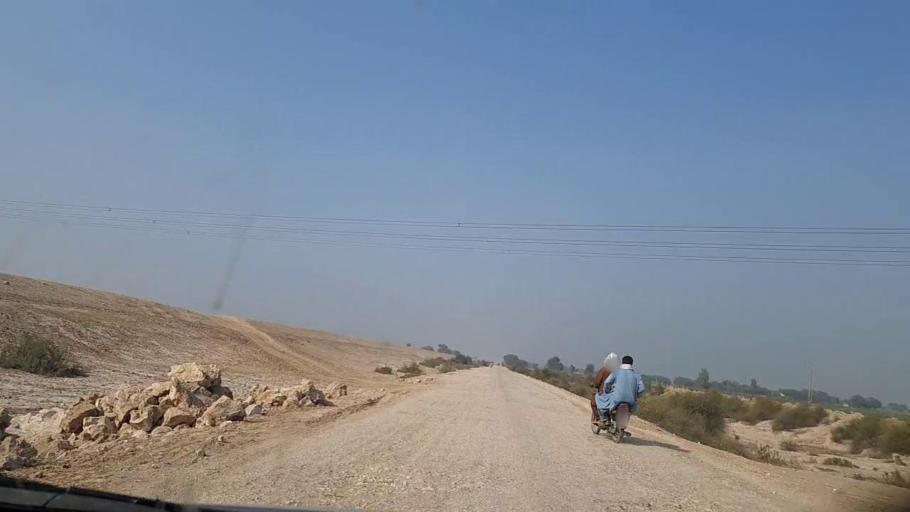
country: PK
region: Sindh
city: Moro
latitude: 26.7110
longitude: 67.9249
